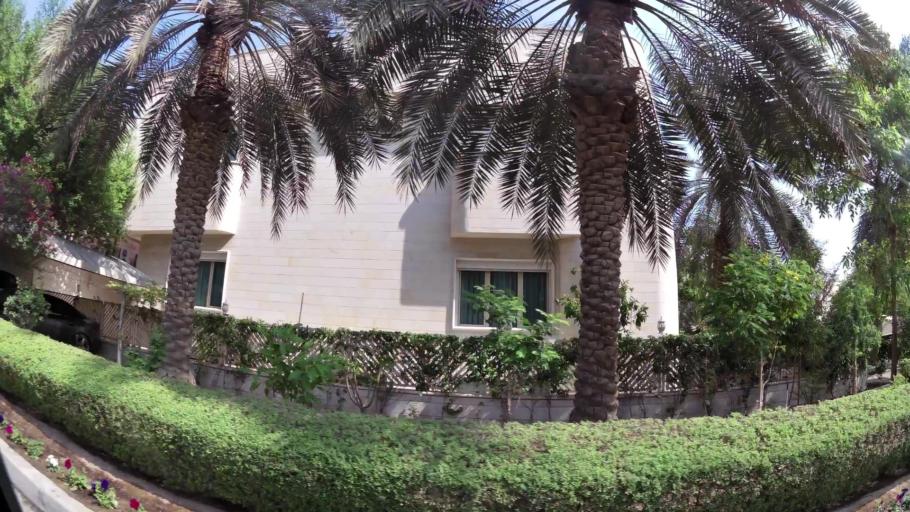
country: KW
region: Al Asimah
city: Ad Dasmah
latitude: 29.3602
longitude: 47.9939
